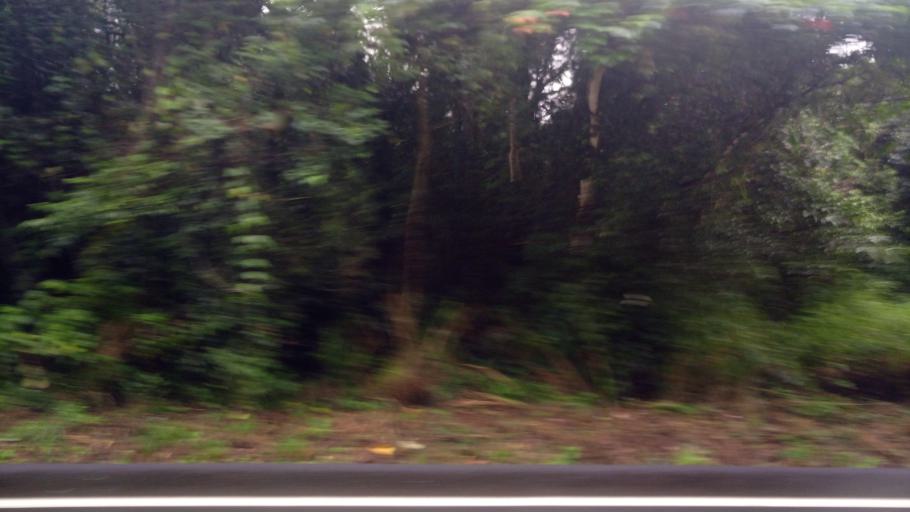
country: AU
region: Queensland
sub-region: Cassowary Coast
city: Innisfail
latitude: -17.6045
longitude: 145.7676
